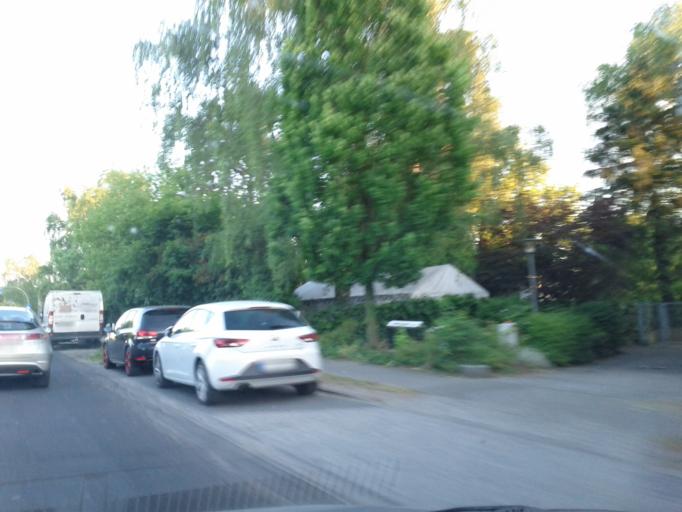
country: DE
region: Brandenburg
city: Hoppegarten
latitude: 52.5220
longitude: 13.6464
